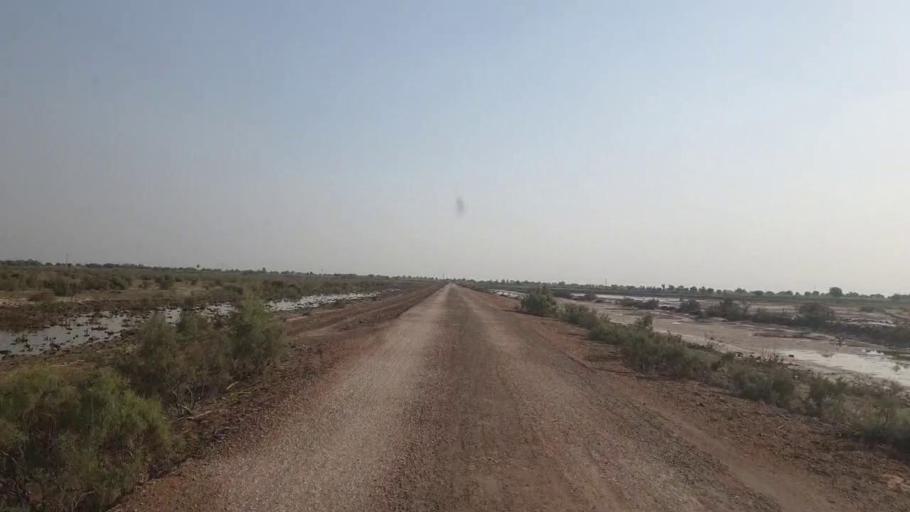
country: PK
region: Sindh
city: Sanghar
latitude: 26.0531
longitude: 68.8969
